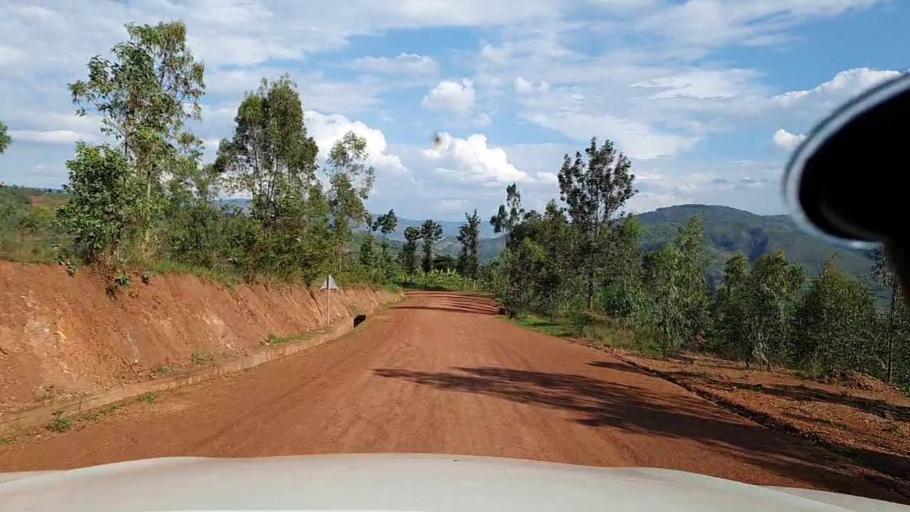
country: RW
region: Kigali
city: Kigali
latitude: -1.8440
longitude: 29.8600
